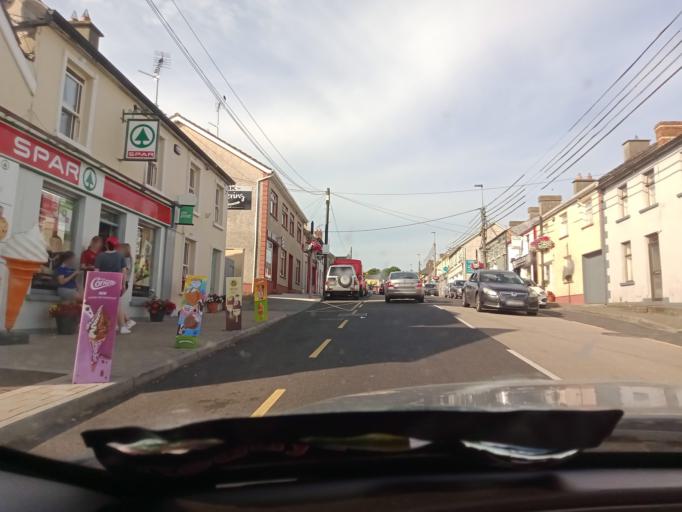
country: IE
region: Ulster
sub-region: An Cabhan
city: Cavan
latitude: 53.9303
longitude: -7.4102
